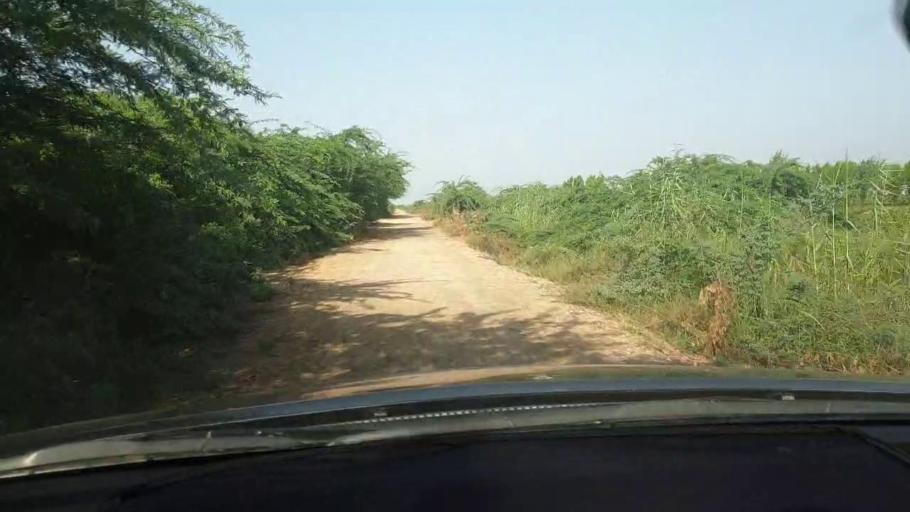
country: PK
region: Sindh
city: Tando Bago
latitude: 24.6740
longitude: 69.1896
